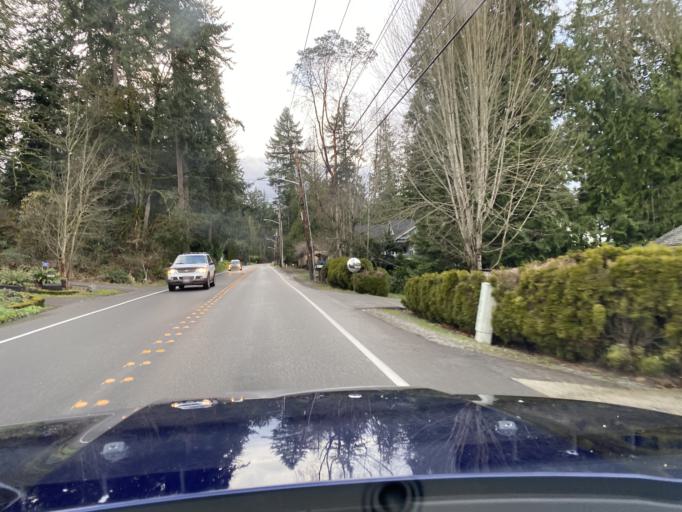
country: US
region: Washington
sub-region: King County
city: West Lake Sammamish
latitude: 47.5703
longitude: -122.1130
